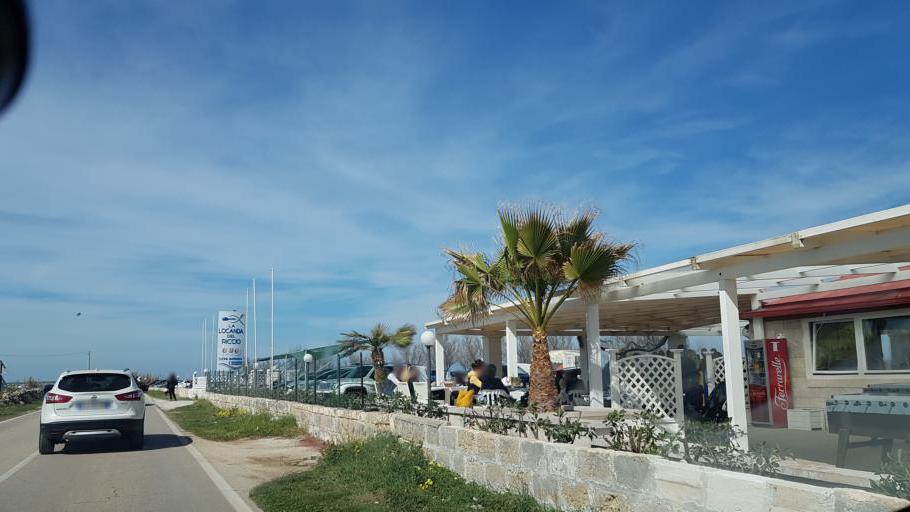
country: IT
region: Apulia
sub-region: Provincia di Brindisi
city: Pezze di Greco
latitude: 40.8554
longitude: 17.4413
